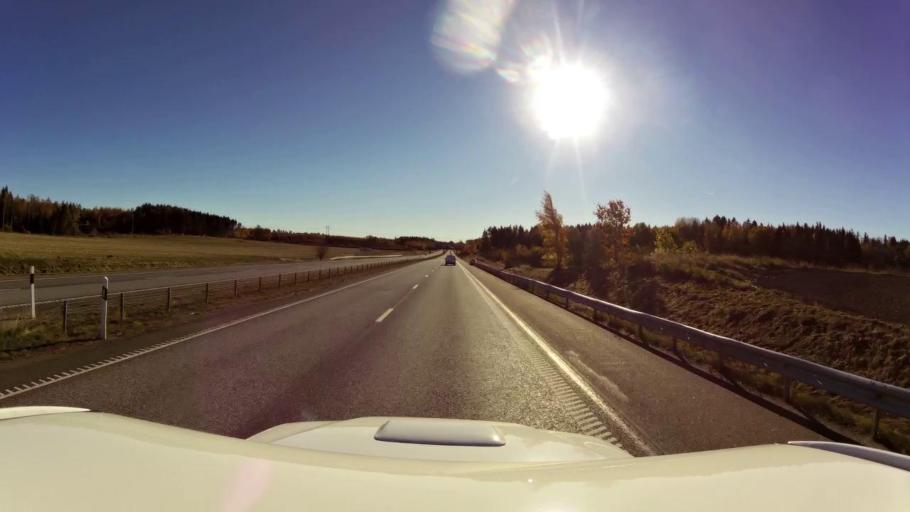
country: SE
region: OEstergoetland
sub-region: Linkopings Kommun
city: Malmslatt
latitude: 58.4192
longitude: 15.5413
